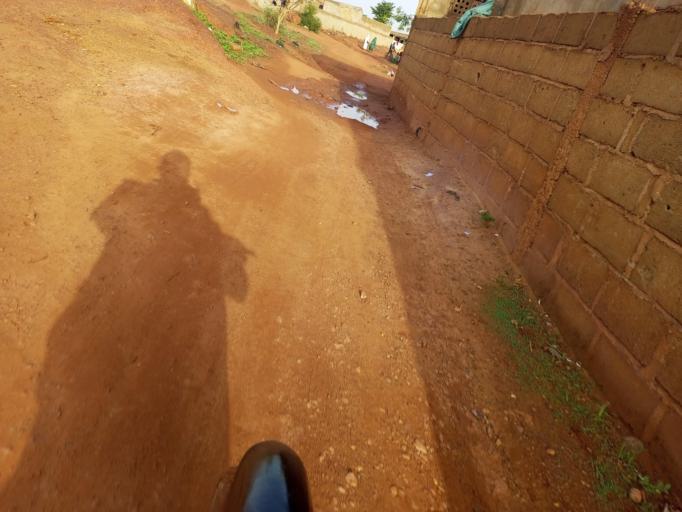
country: ML
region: Bamako
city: Bamako
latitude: 12.5204
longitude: -7.9913
